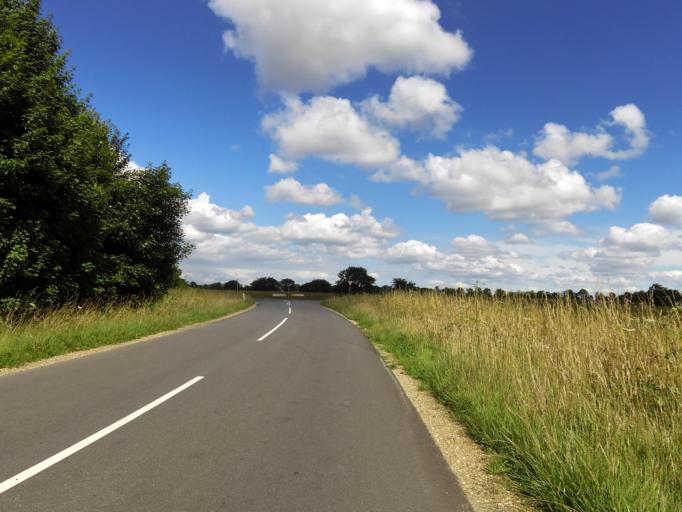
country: DK
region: South Denmark
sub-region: Haderslev Kommune
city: Gram
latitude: 55.3135
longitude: 9.1169
